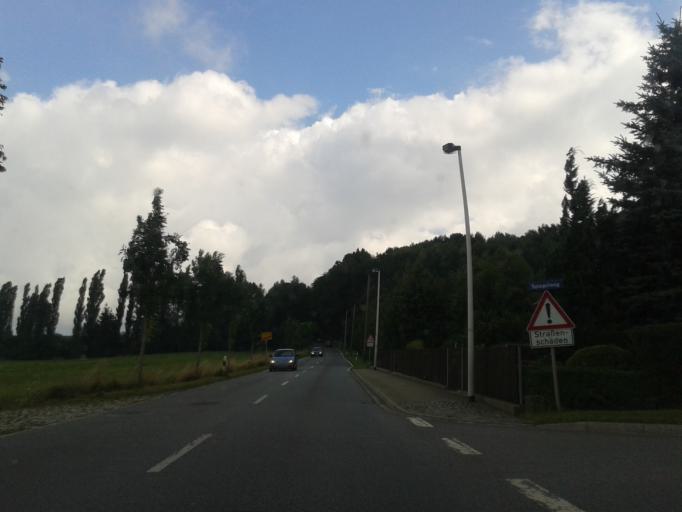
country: DE
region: Saxony
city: Durrrohrsdorf
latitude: 51.0440
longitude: 13.9340
